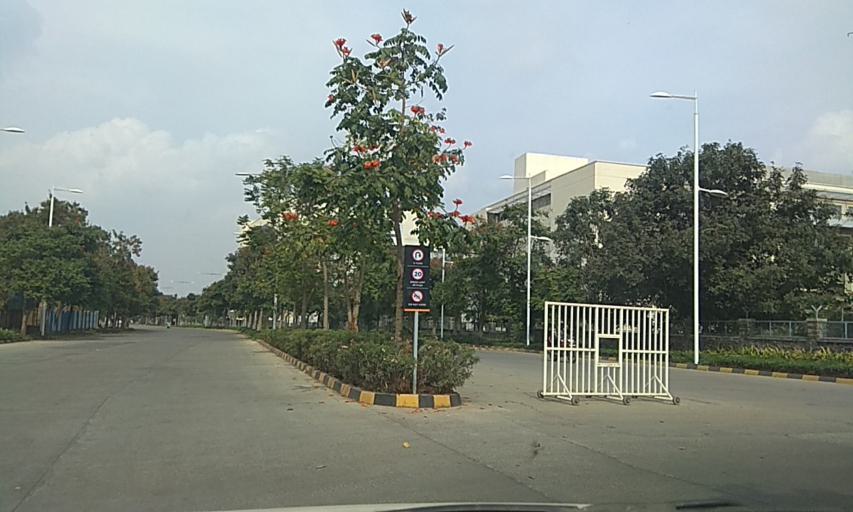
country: IN
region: Maharashtra
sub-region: Pune Division
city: Pimpri
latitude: 18.6032
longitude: 73.7150
